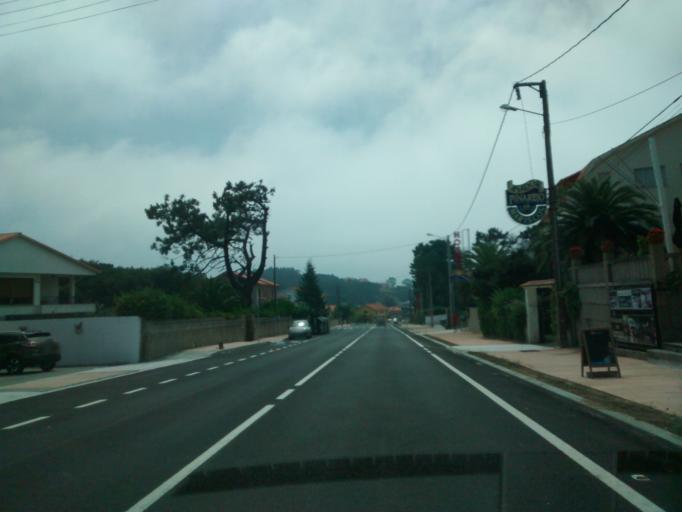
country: ES
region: Galicia
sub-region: Provincia de Pontevedra
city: Sanxenxo
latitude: 42.4206
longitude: -8.8724
